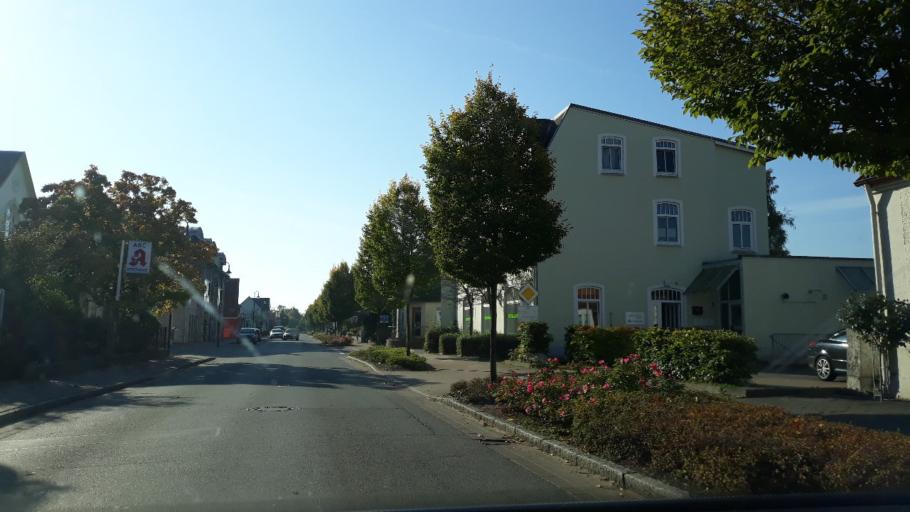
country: DE
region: Schleswig-Holstein
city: Boklund
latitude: 54.6038
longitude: 9.5837
